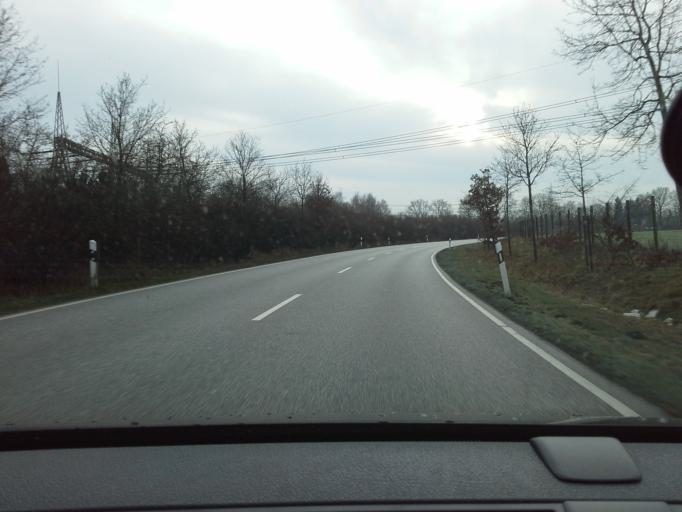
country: DE
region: Schleswig-Holstein
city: Henstedt-Ulzburg
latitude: 53.7422
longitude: 9.9822
